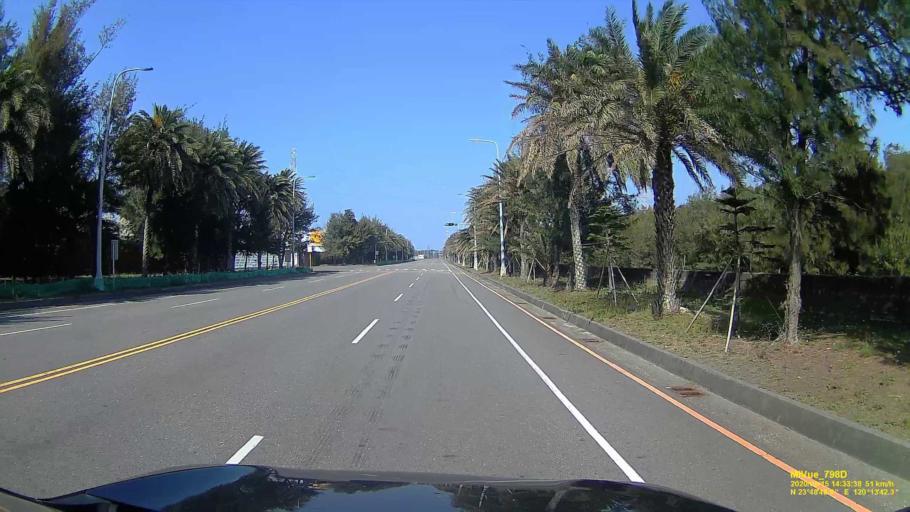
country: TW
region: Taiwan
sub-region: Yunlin
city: Douliu
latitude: 23.8137
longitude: 120.2285
